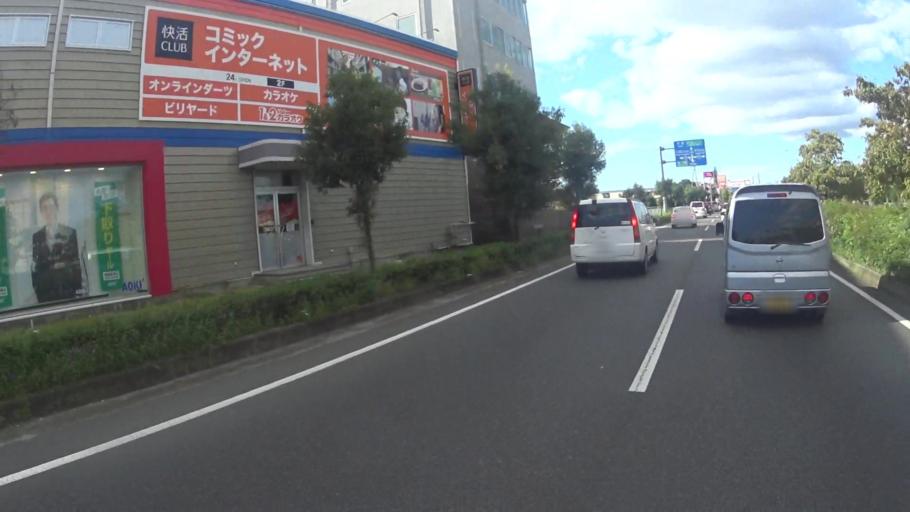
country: JP
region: Kyoto
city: Uji
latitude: 34.8691
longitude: 135.7619
